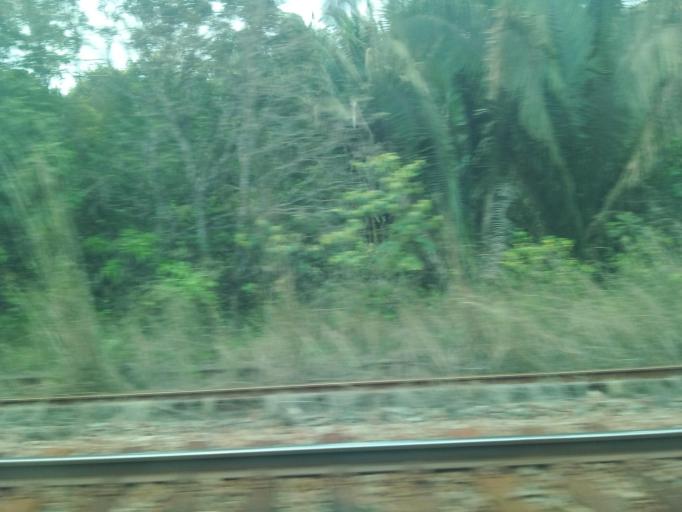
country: BR
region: Maranhao
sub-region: Santa Ines
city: Santa Ines
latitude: -3.6525
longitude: -45.7981
